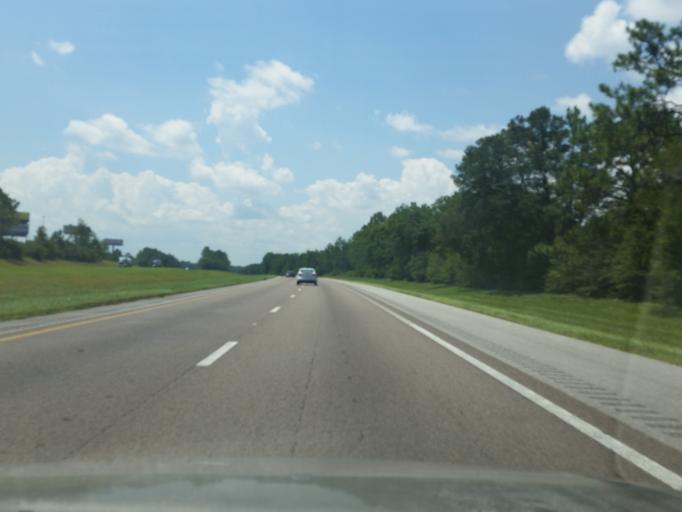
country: US
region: Alabama
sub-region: Baldwin County
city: Robertsdale
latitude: 30.6150
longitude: -87.5740
